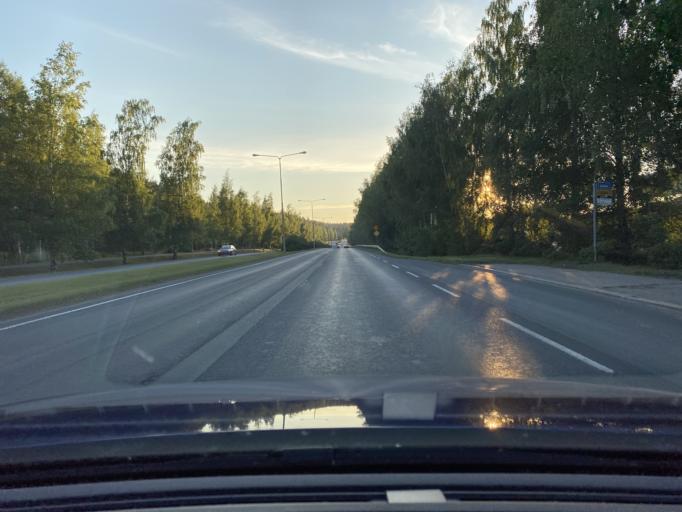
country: FI
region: Pirkanmaa
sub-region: Tampere
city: Pirkkala
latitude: 61.5122
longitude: 23.6758
